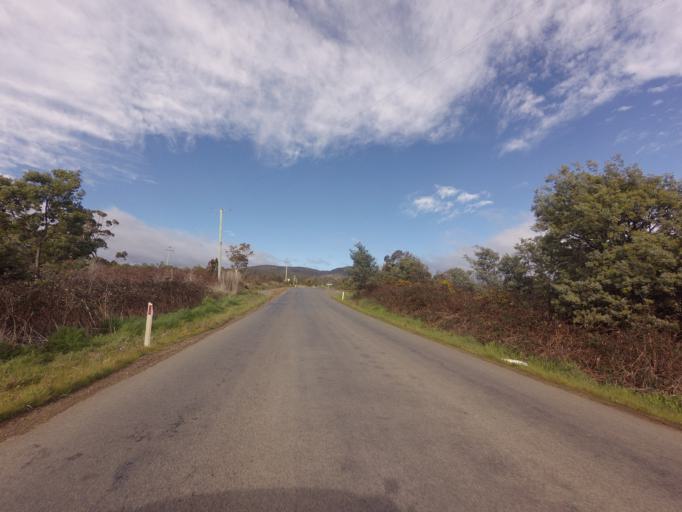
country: AU
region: Tasmania
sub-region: Derwent Valley
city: New Norfolk
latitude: -42.7770
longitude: 147.0202
